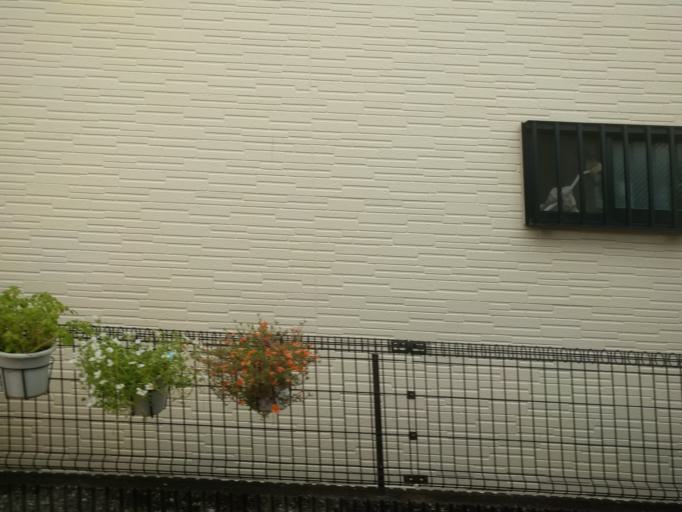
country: JP
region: Saitama
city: Shimotoda
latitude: 35.8285
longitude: 139.6772
